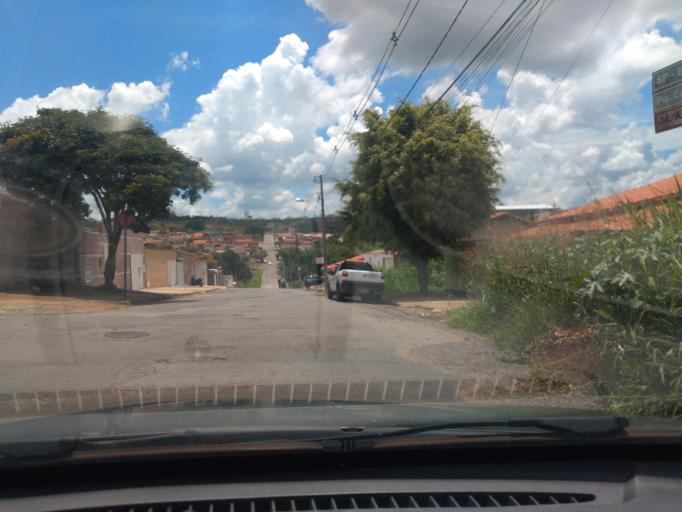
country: BR
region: Minas Gerais
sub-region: Tres Coracoes
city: Tres Coracoes
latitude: -21.6783
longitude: -45.2705
